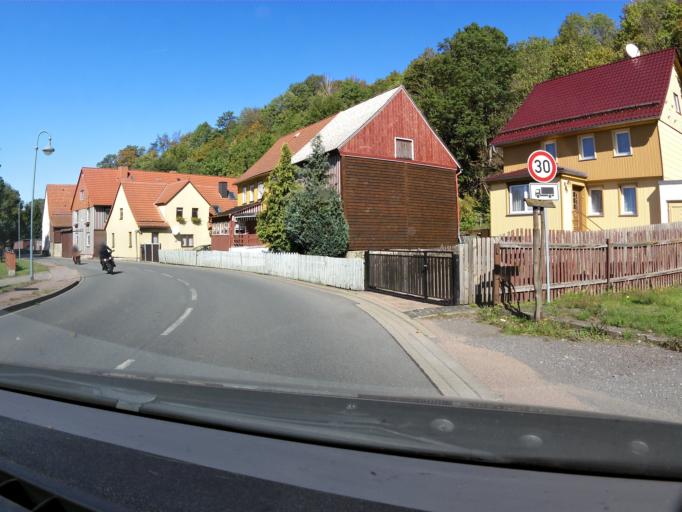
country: DE
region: Saxony-Anhalt
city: Hasselfelde
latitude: 51.6675
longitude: 10.8866
